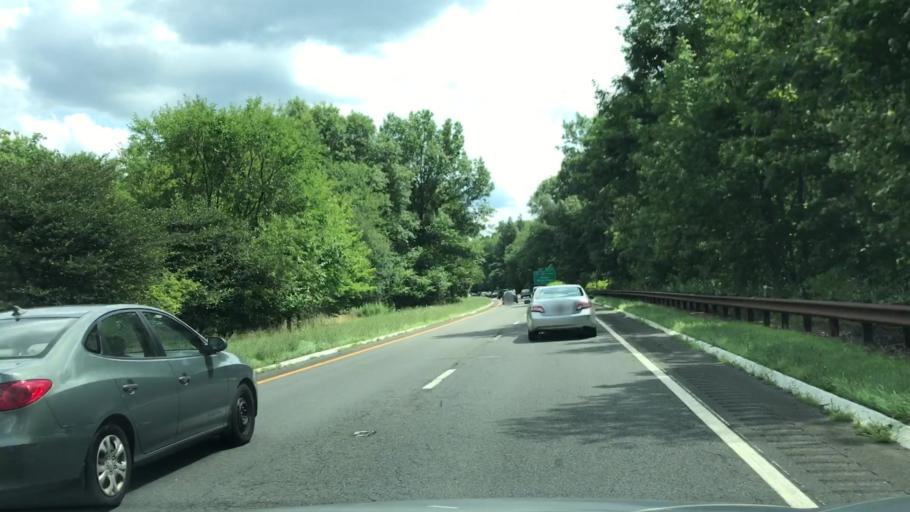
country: US
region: New York
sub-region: Rockland County
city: Bardonia
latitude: 41.1138
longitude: -74.0025
